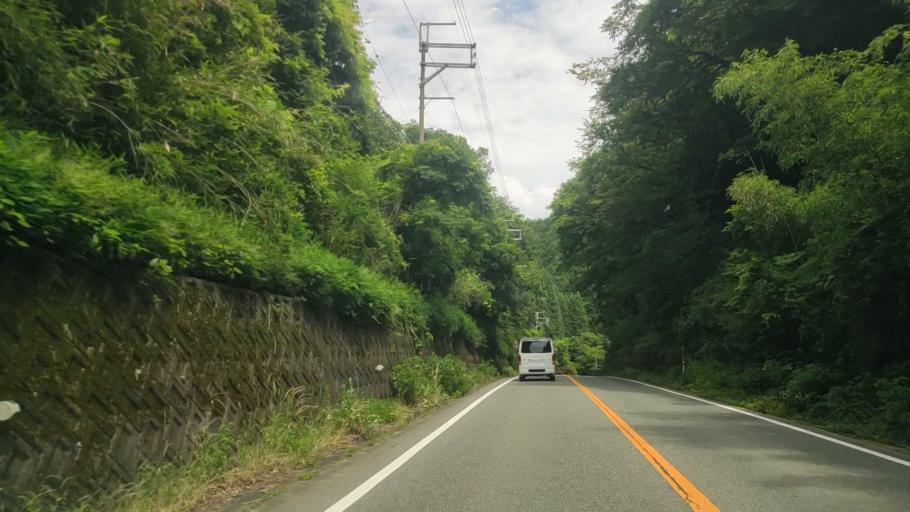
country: JP
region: Hyogo
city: Yamazakicho-nakabirose
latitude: 34.9896
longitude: 134.4095
